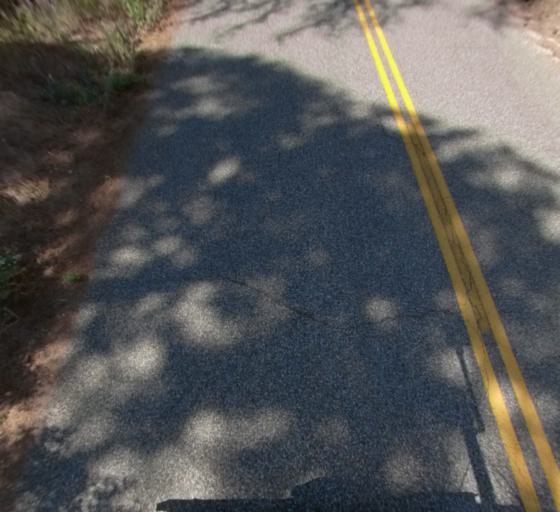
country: US
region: California
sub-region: Madera County
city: Oakhurst
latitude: 37.3940
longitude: -119.3523
